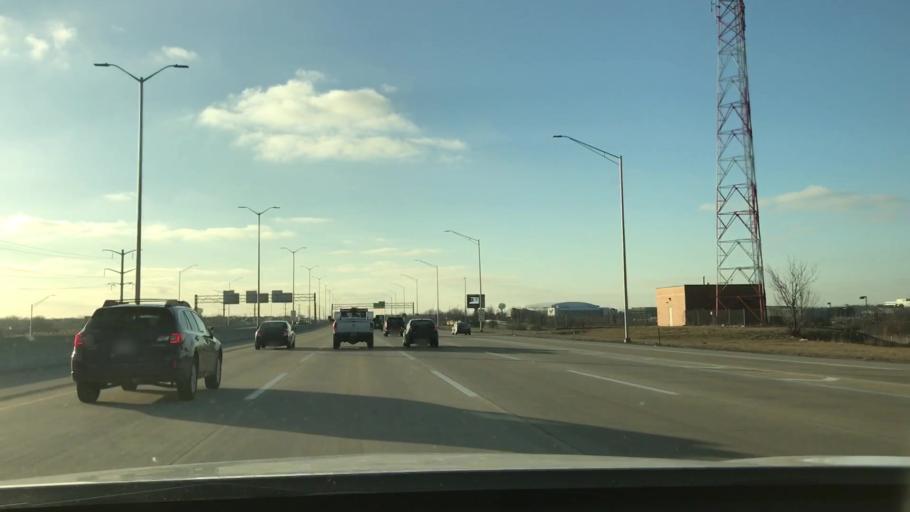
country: US
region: Illinois
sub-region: Cook County
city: Streamwood
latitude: 42.0670
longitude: -88.1974
